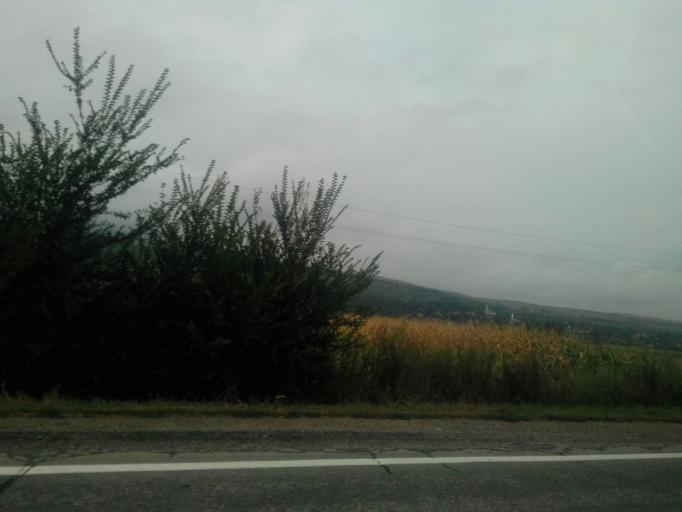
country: RO
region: Cluj
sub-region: Comuna Mihai Viteazu
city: Mihai Viteazu
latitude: 46.5304
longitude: 23.7090
